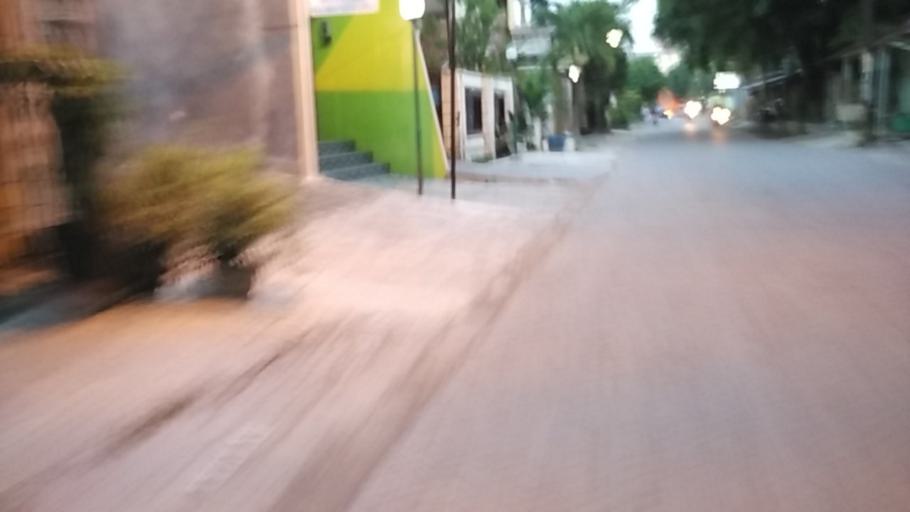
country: ID
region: Central Java
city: Semarang
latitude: -6.9826
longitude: 110.4578
